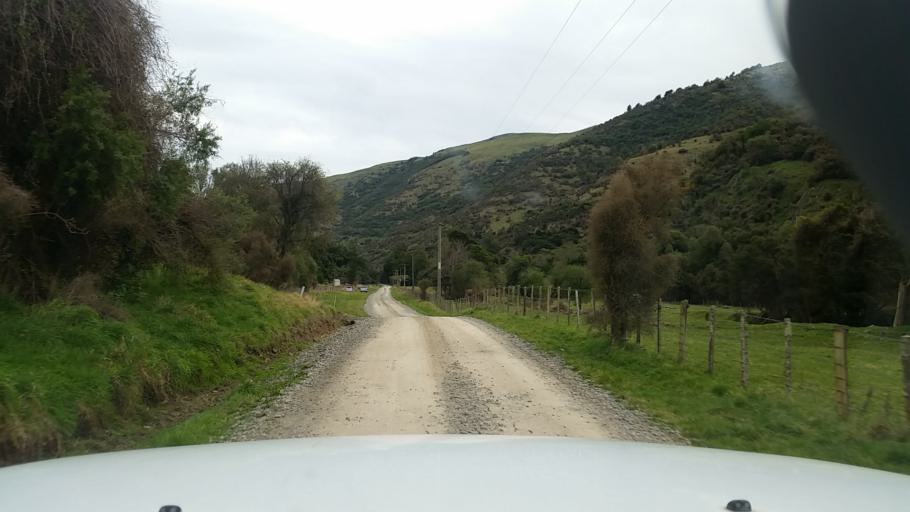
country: NZ
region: Canterbury
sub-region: Christchurch City
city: Christchurch
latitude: -43.7640
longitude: 172.7201
